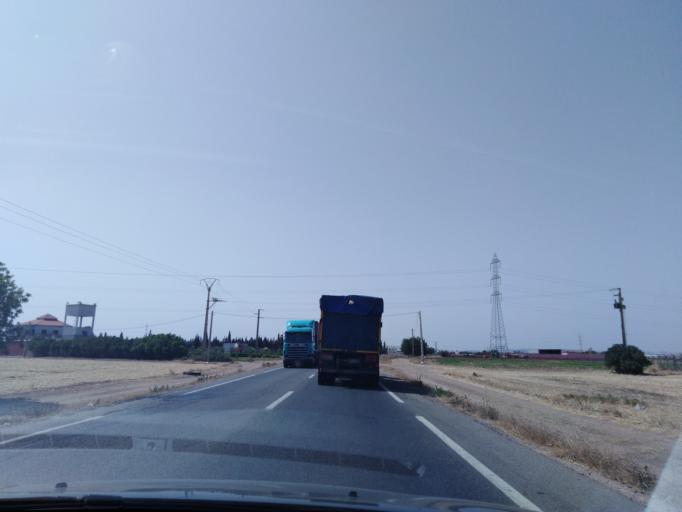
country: MA
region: Chaouia-Ouardigha
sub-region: Settat Province
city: Berrechid
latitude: 33.1545
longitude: -7.6195
